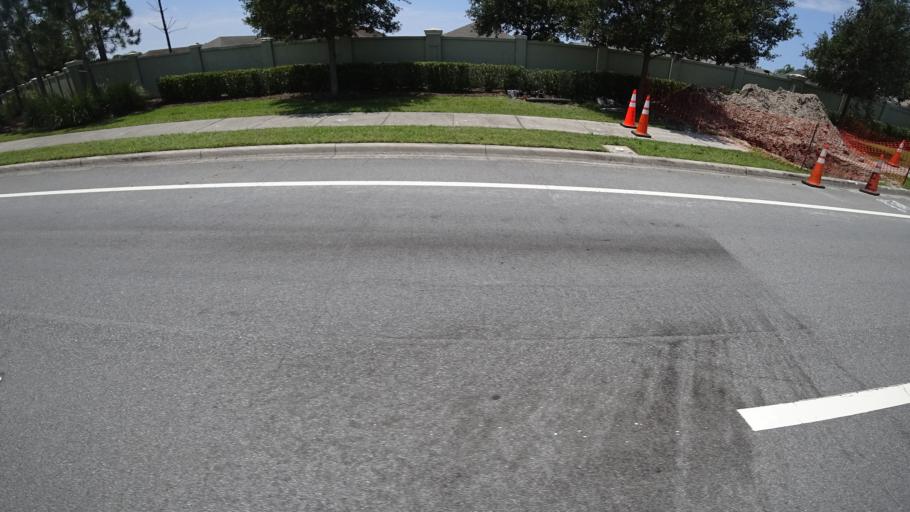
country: US
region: Florida
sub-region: Sarasota County
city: North Sarasota
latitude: 27.4275
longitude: -82.5003
